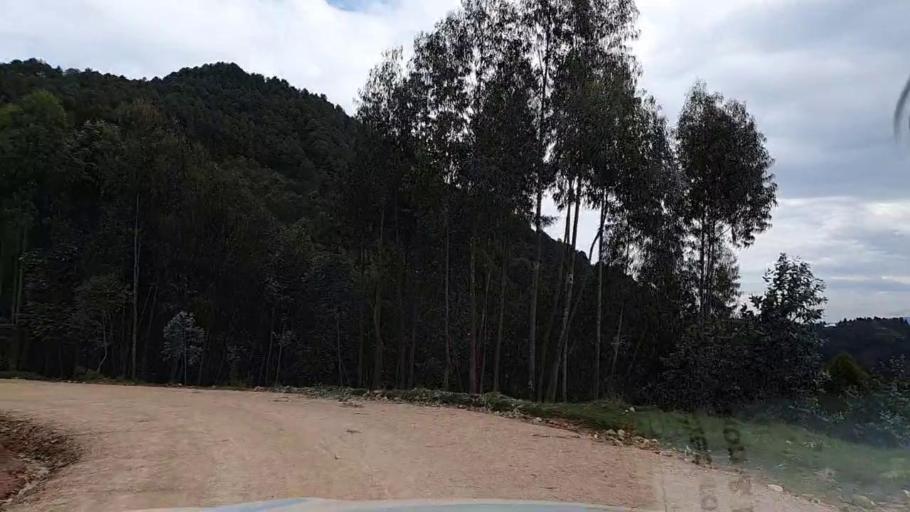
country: RW
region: Southern Province
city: Nzega
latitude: -2.4035
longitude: 29.4538
